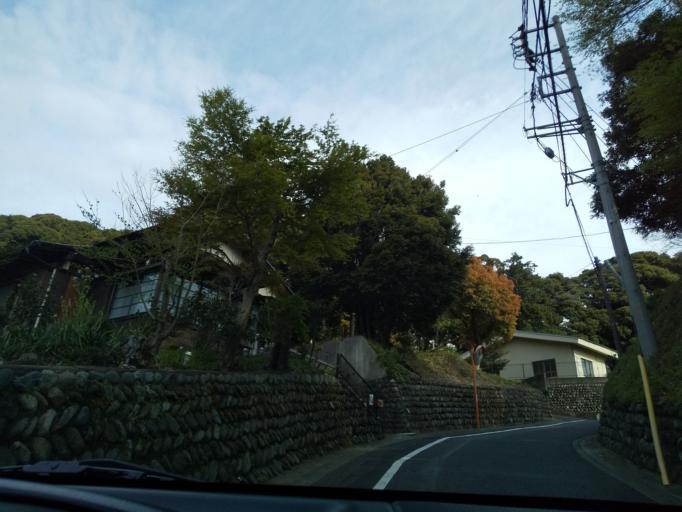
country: JP
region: Tokyo
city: Hino
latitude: 35.6528
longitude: 139.4275
